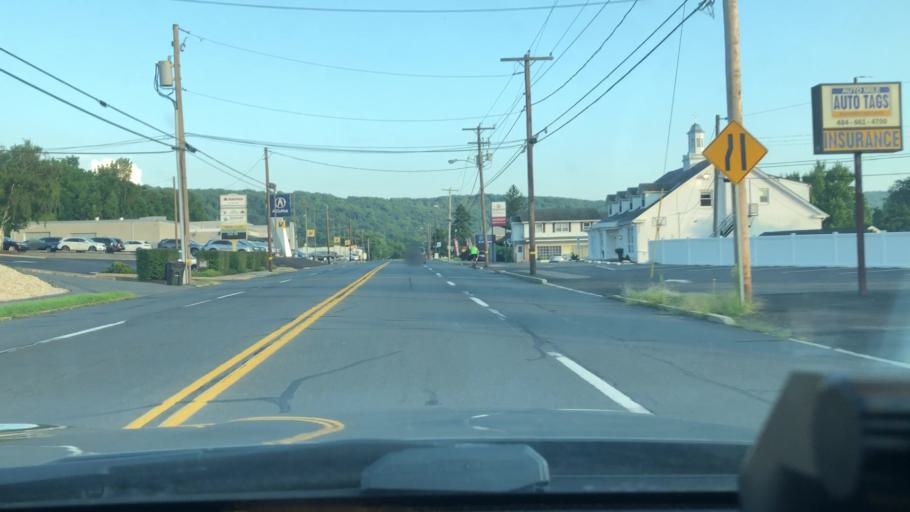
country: US
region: Pennsylvania
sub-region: Lehigh County
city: Emmaus
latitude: 40.5469
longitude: -75.4892
